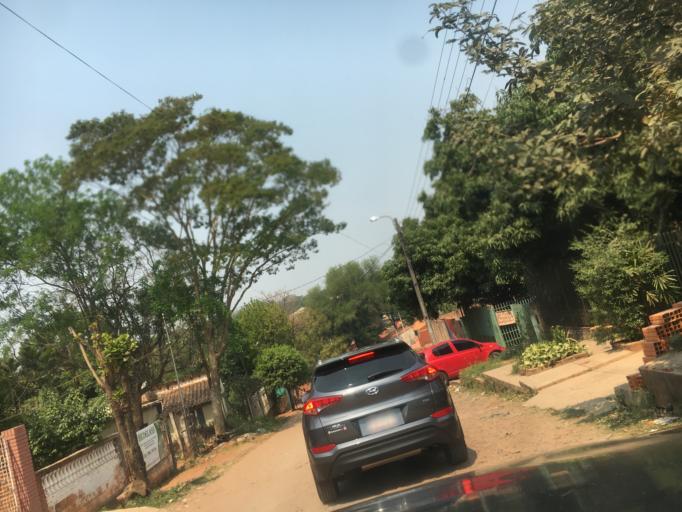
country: PY
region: Central
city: Villa Elisa
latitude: -25.3609
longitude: -57.5913
